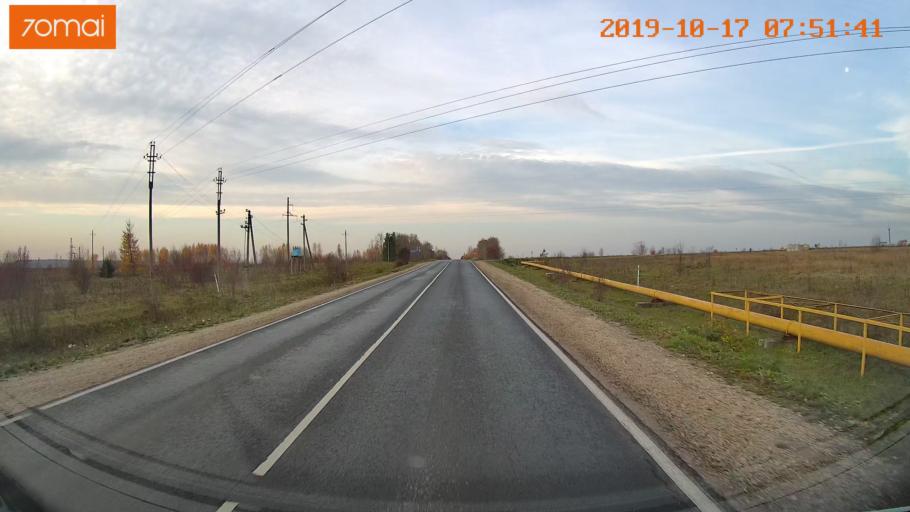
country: RU
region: Vladimir
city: Yur'yev-Pol'skiy
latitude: 56.4797
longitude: 39.6526
